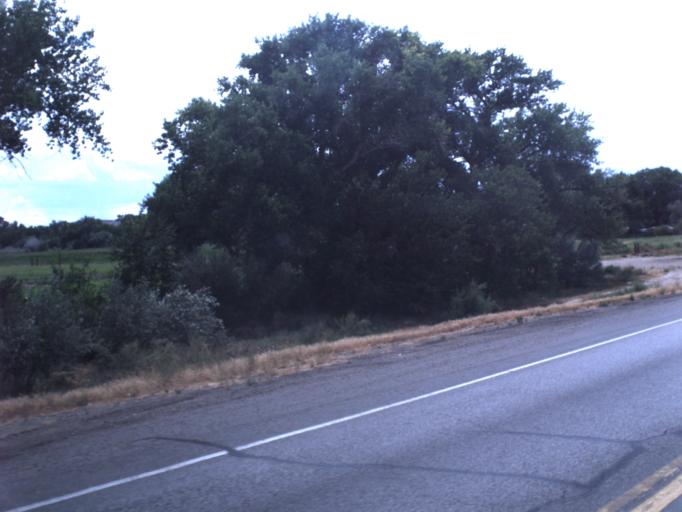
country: US
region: Utah
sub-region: Carbon County
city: East Carbon City
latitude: 38.9942
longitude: -110.1451
